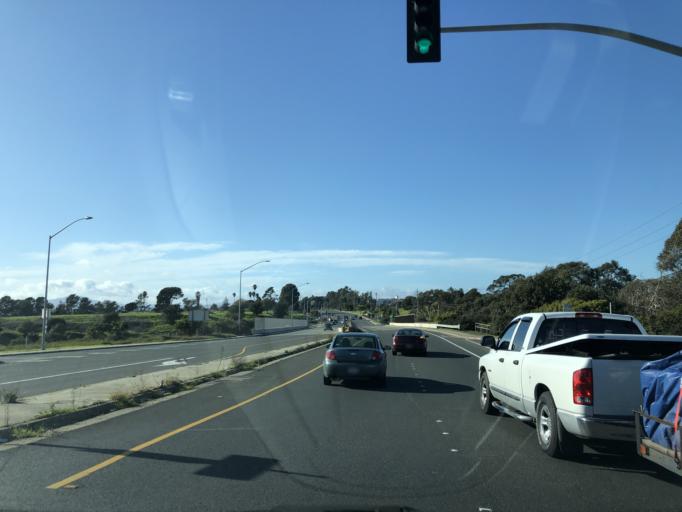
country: US
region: California
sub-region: Contra Costa County
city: Rollingwood
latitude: 37.9760
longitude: -122.3168
